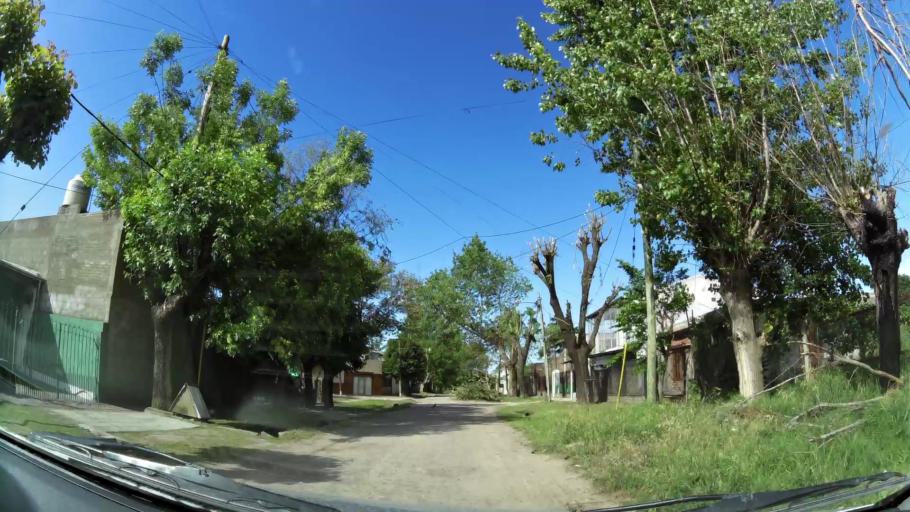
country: AR
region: Buenos Aires
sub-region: Partido de Almirante Brown
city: Adrogue
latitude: -34.8039
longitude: -58.3570
